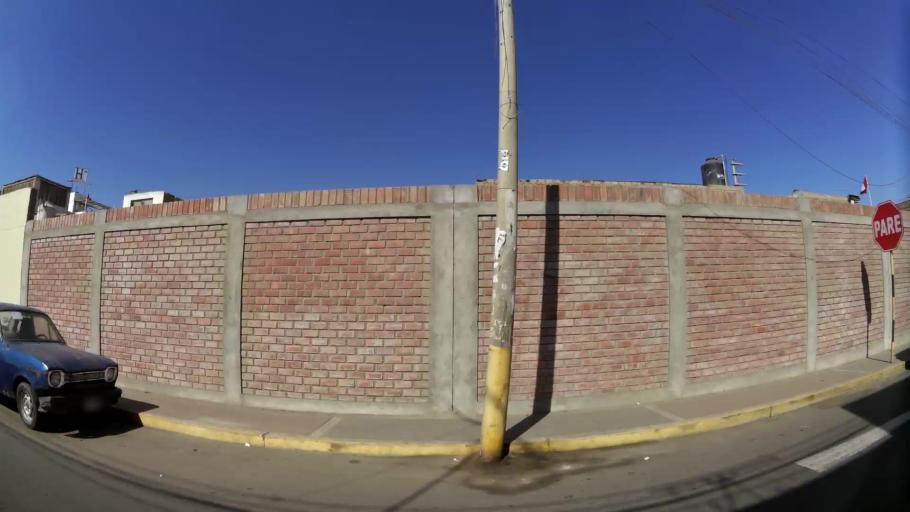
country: PE
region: Ica
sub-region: Provincia de Chincha
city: Chincha Alta
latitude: -13.4174
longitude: -76.1308
